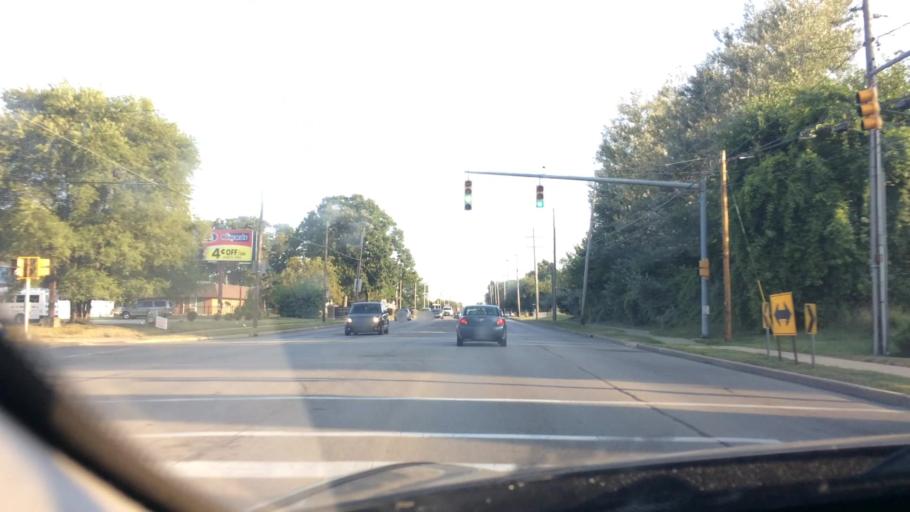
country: US
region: Ohio
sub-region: Lucas County
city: Ottawa Hills
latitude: 41.6457
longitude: -83.6260
